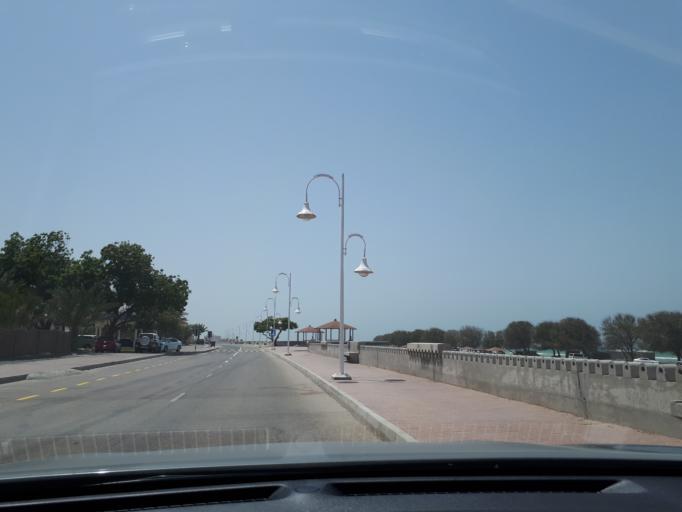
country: OM
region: Muhafazat Masqat
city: As Sib al Jadidah
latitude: 23.7122
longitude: 58.0747
